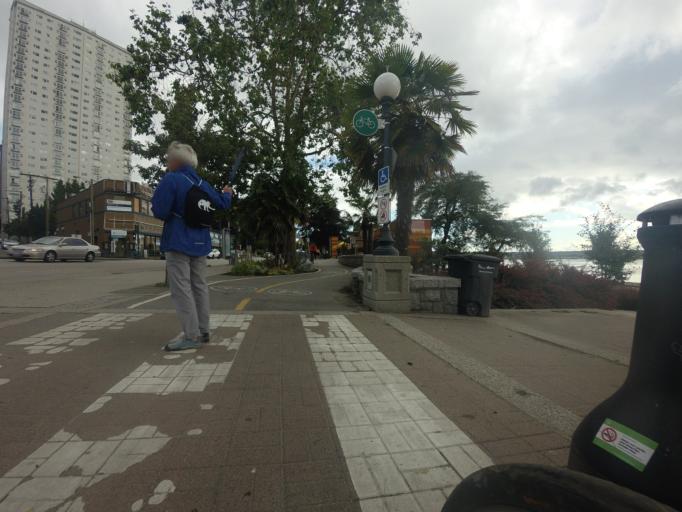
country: CA
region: British Columbia
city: West End
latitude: 49.2871
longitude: -123.1426
